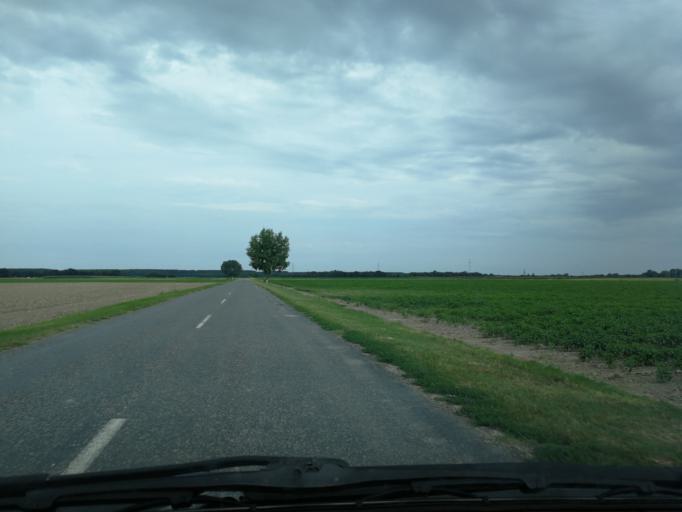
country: HU
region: Bacs-Kiskun
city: Batya
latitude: 46.4512
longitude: 18.9666
